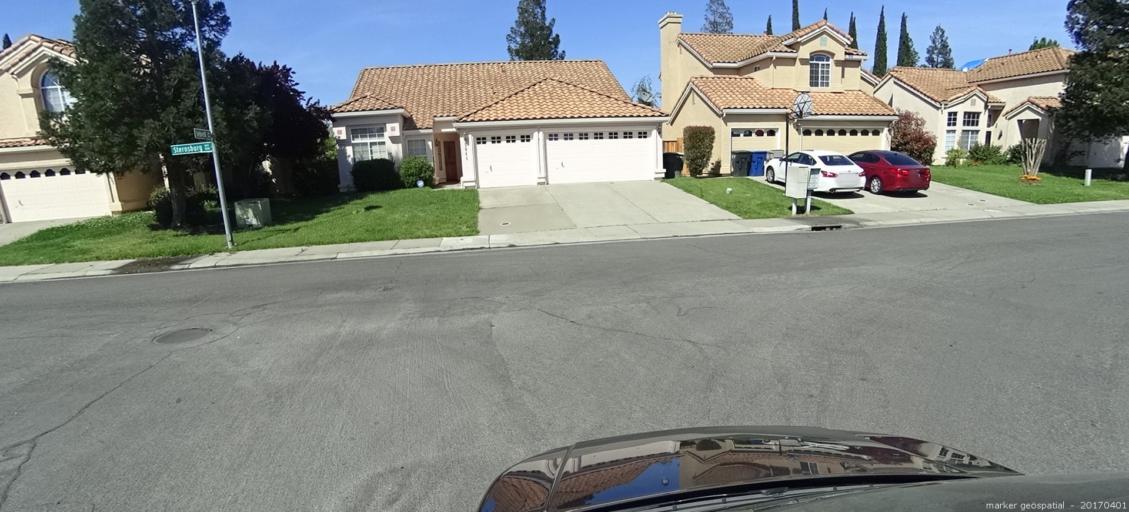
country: US
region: California
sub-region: Sacramento County
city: Laguna
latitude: 38.4447
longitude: -121.4358
